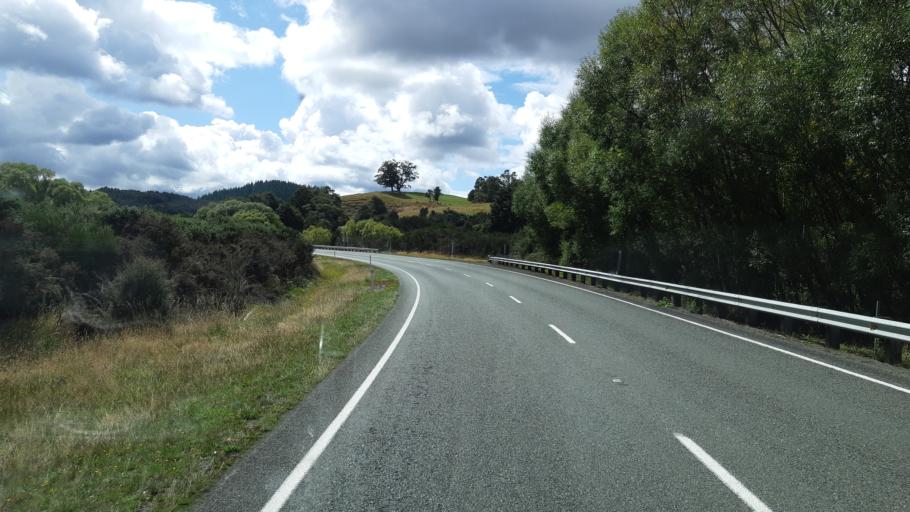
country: NZ
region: Tasman
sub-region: Tasman District
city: Wakefield
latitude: -41.6454
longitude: 172.6570
